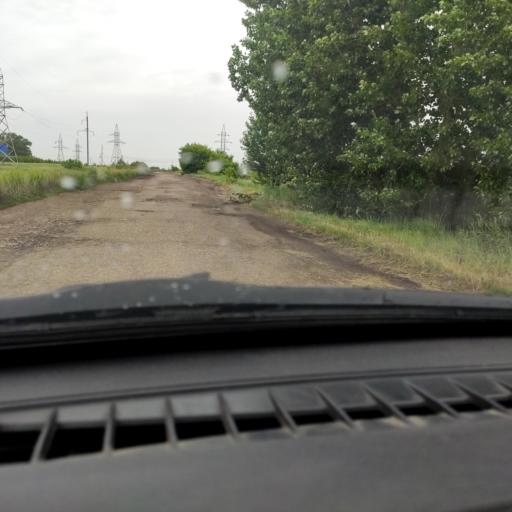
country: RU
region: Samara
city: Tol'yatti
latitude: 53.5865
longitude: 49.4108
